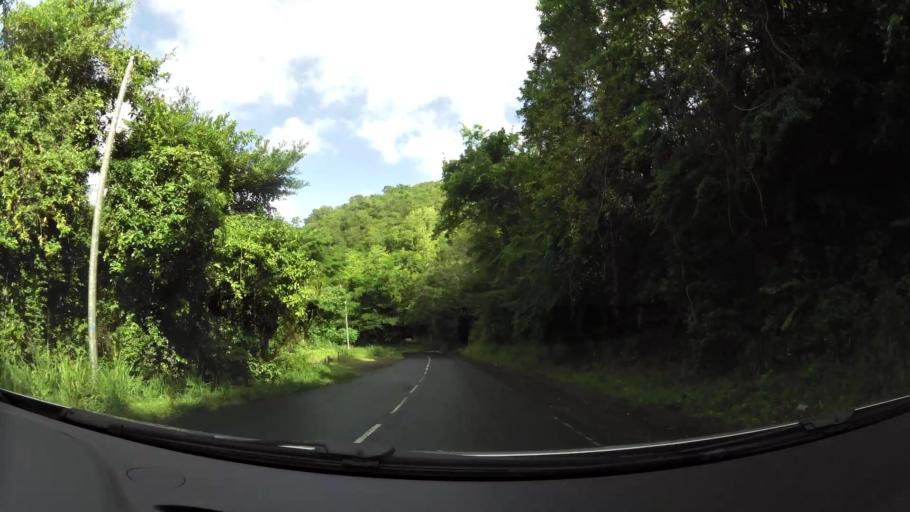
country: MQ
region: Martinique
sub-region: Martinique
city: Les Trois-Ilets
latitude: 14.5373
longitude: -61.0549
